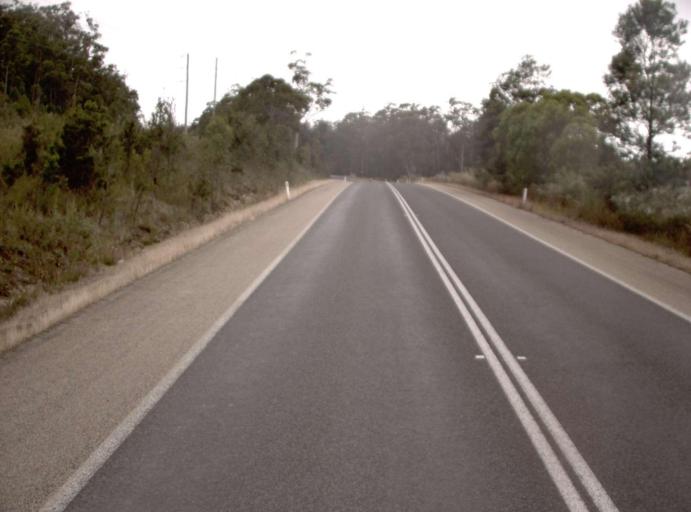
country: AU
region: Victoria
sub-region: East Gippsland
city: Lakes Entrance
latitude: -37.7272
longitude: 147.8916
